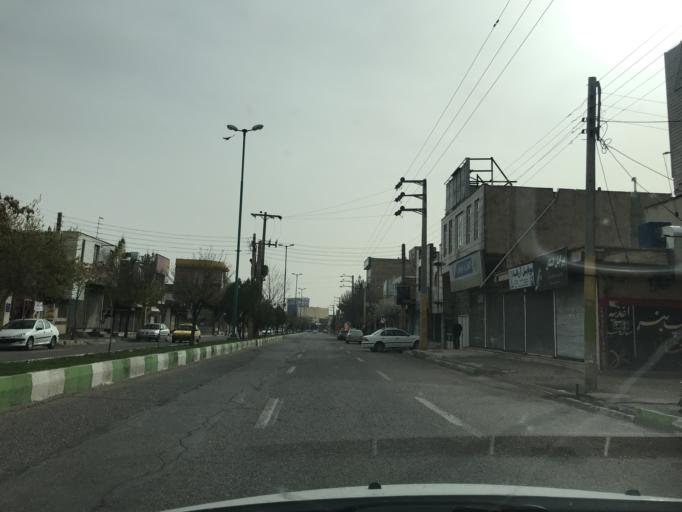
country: IR
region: Qazvin
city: Takestan
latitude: 36.0666
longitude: 49.6928
